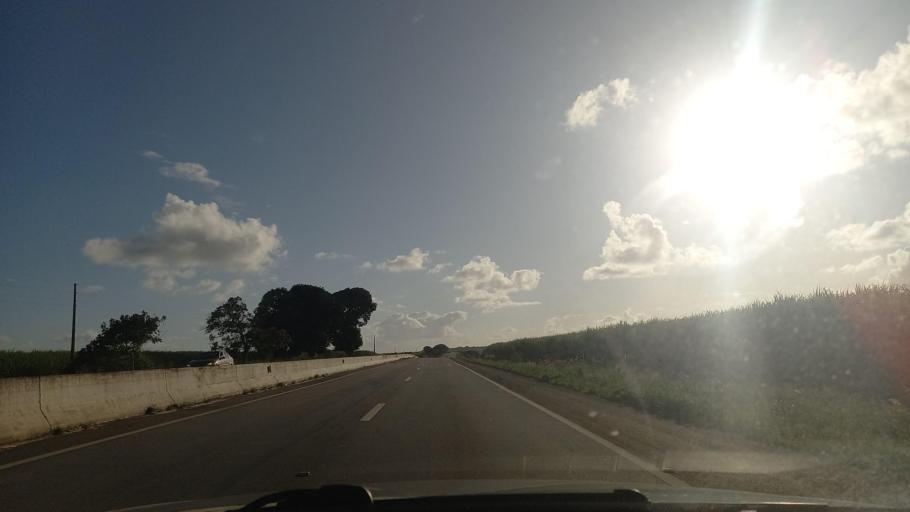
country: BR
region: Alagoas
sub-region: Sao Miguel Dos Campos
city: Sao Miguel dos Campos
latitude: -9.8005
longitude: -36.1799
